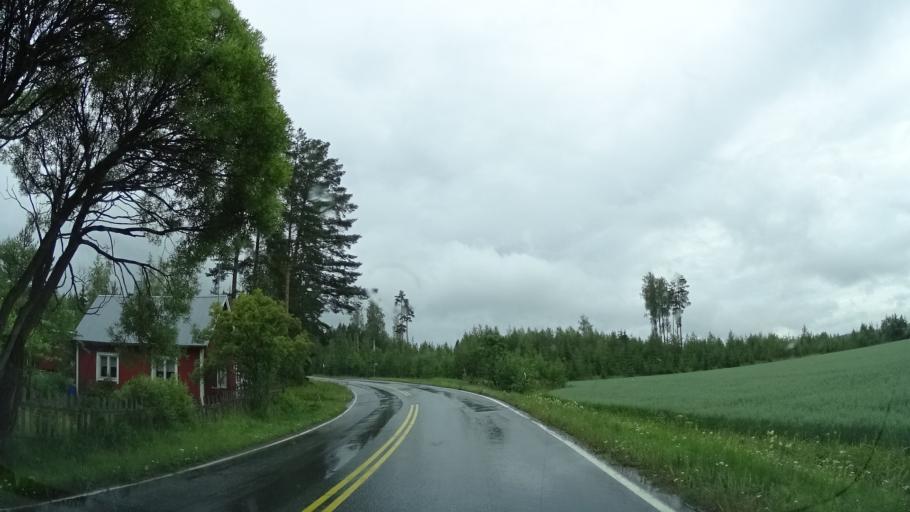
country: FI
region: Haeme
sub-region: Forssa
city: Humppila
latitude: 60.9982
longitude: 23.2544
